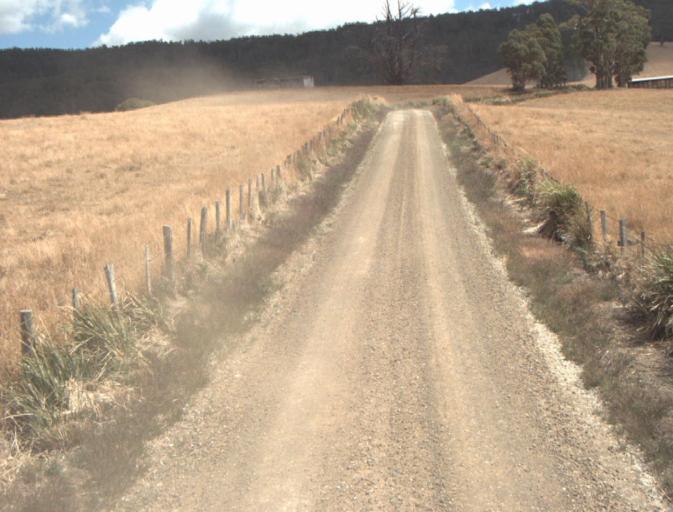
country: AU
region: Tasmania
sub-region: Launceston
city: Mayfield
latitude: -41.2259
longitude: 147.1196
